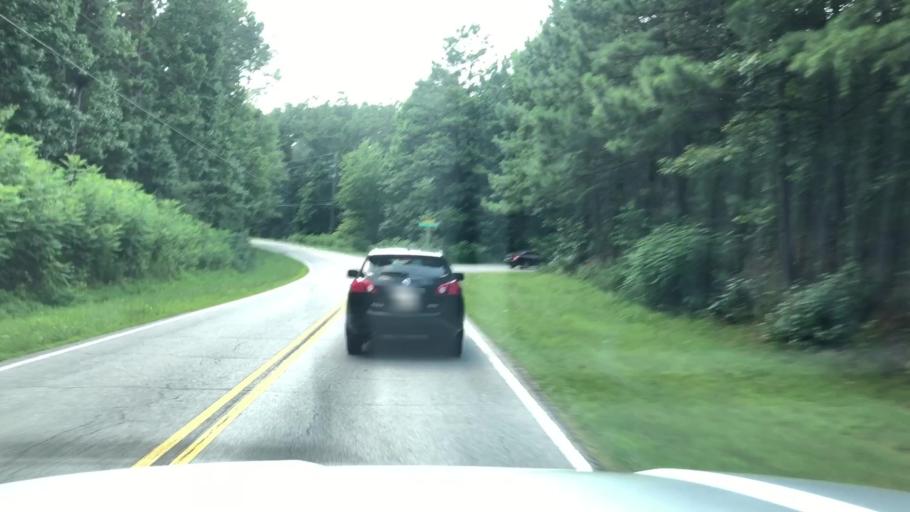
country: US
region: Georgia
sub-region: Paulding County
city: Dallas
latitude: 33.9745
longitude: -84.8187
